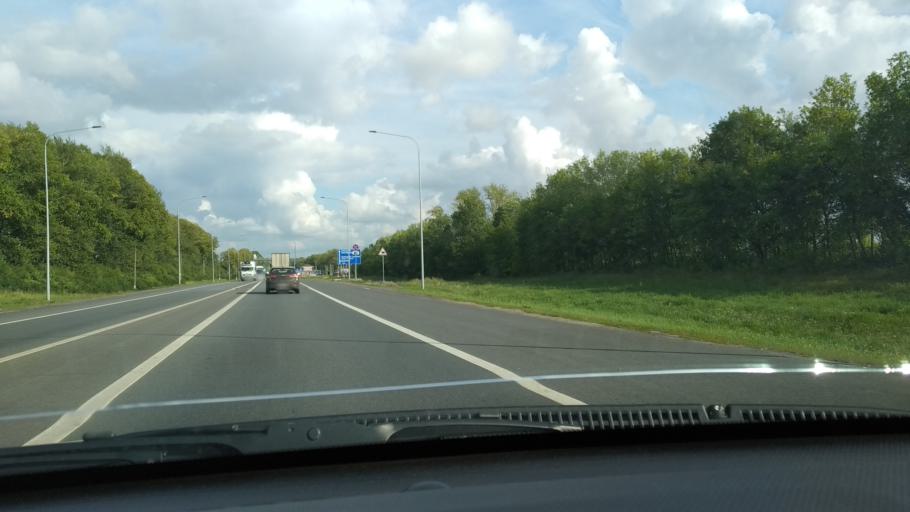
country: RU
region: Tatarstan
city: Stolbishchi
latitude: 55.6581
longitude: 49.3060
